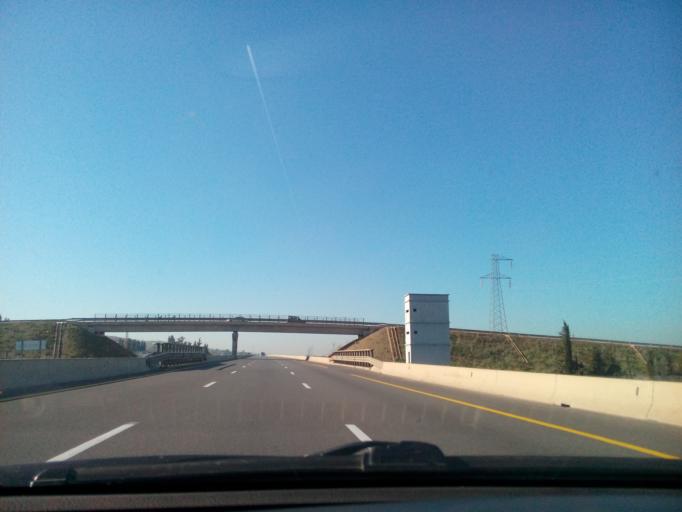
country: DZ
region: Chlef
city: Boukadir
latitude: 36.0411
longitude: 1.0929
